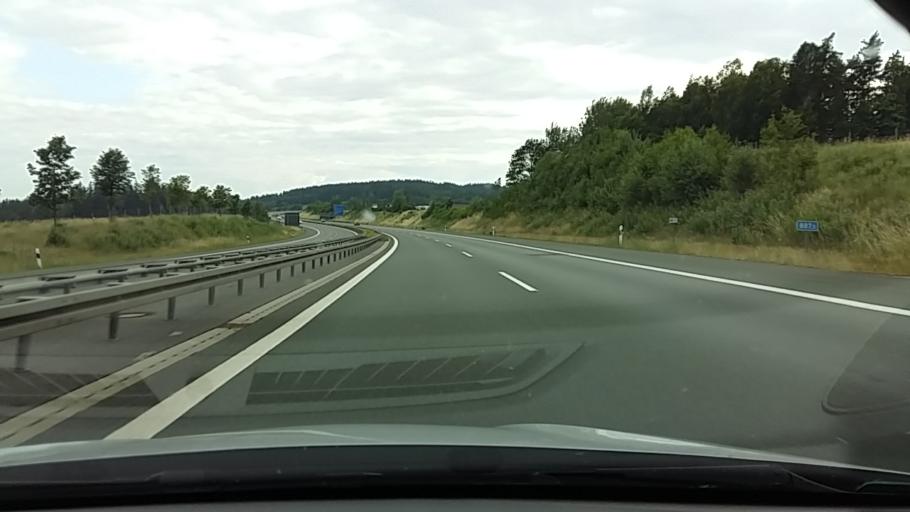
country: DE
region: Bavaria
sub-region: Upper Palatinate
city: Leuchtenberg
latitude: 49.5847
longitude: 12.2794
